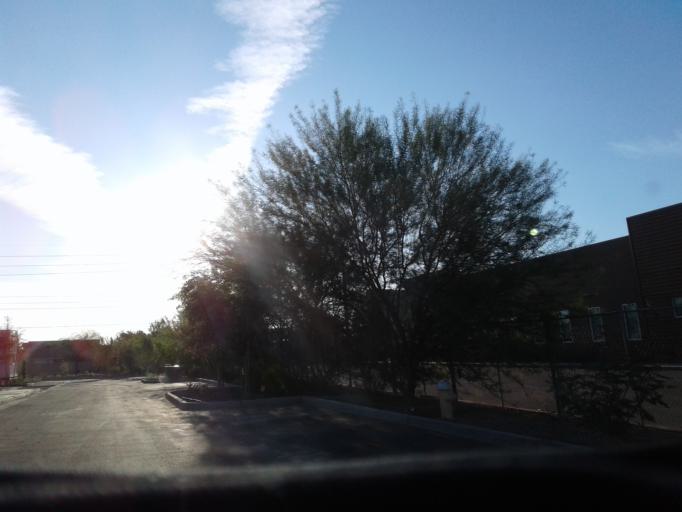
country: US
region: Arizona
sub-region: Maricopa County
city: Paradise Valley
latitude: 33.5943
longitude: -112.0144
